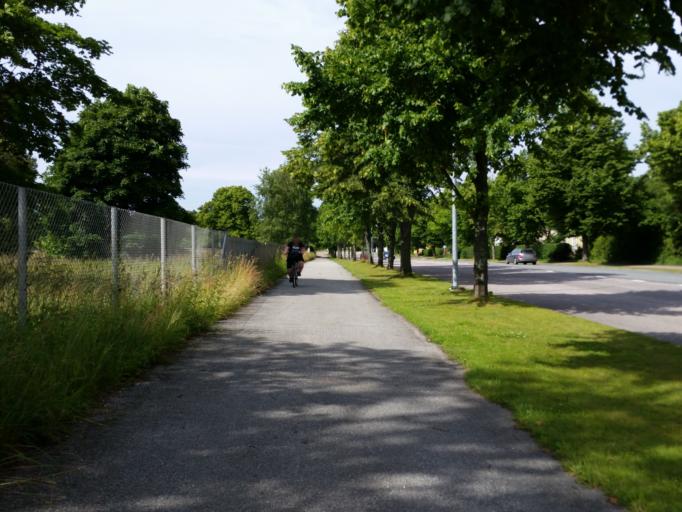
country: FI
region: Uusimaa
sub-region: Raaseporin
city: Hanko
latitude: 59.8286
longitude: 22.9530
